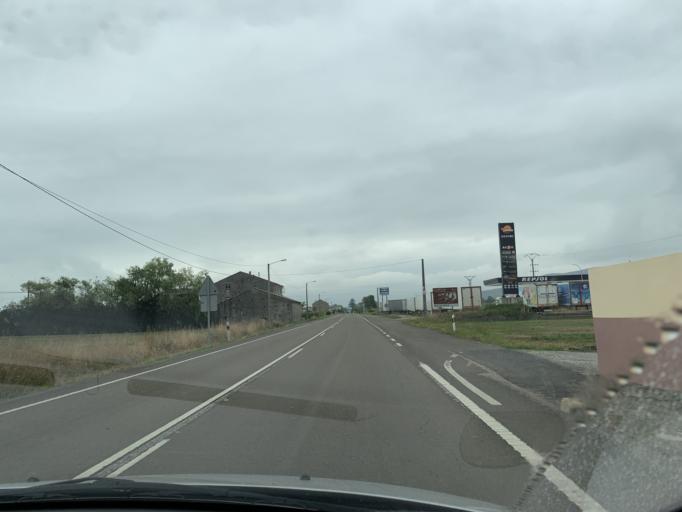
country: ES
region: Galicia
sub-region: Provincia de Lugo
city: Barreiros
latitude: 43.5497
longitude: -7.1391
